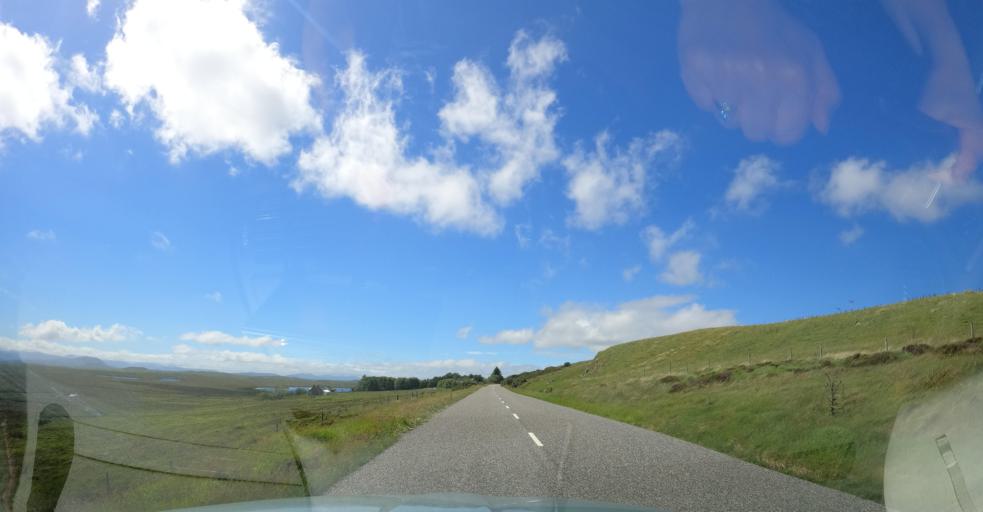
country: GB
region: Scotland
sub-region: Eilean Siar
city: Stornoway
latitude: 58.1656
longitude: -6.5555
